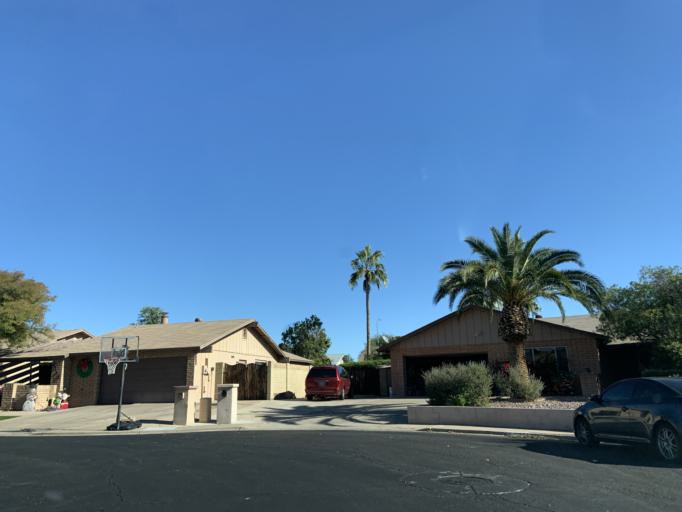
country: US
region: Arizona
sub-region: Maricopa County
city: San Carlos
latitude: 33.3720
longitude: -111.8623
